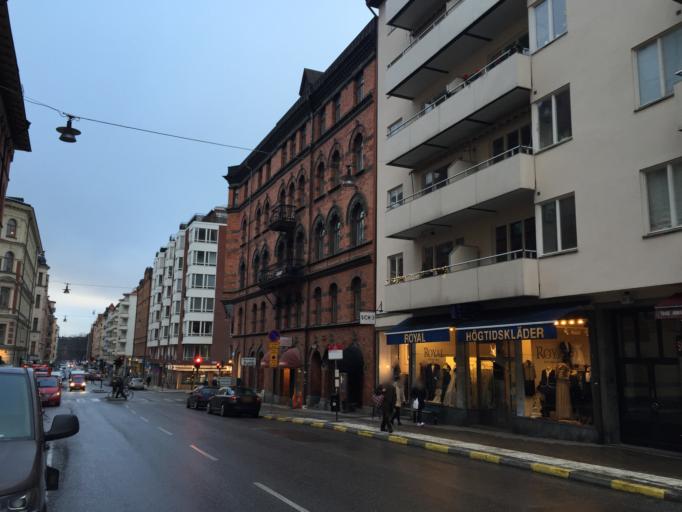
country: SE
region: Stockholm
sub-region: Stockholms Kommun
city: OEstermalm
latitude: 59.3370
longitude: 18.0818
